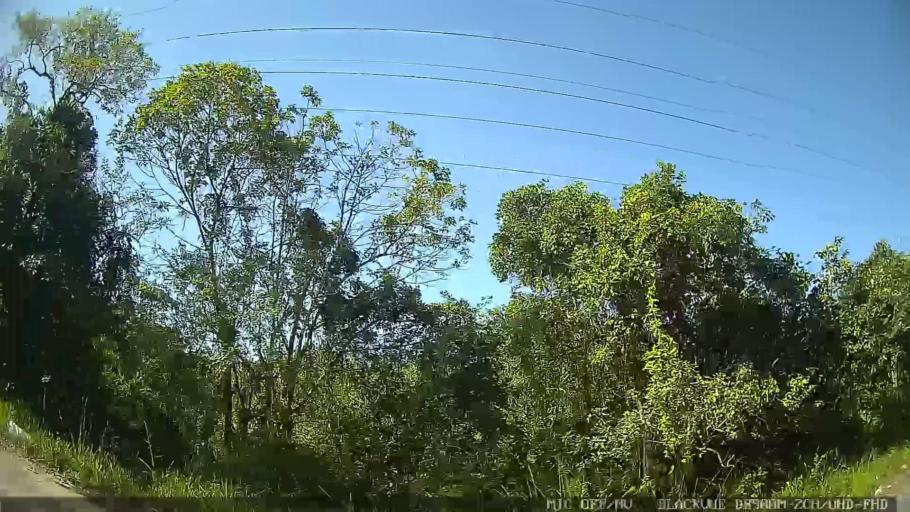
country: BR
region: Sao Paulo
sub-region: Santos
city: Santos
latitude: -23.8993
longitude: -46.3019
